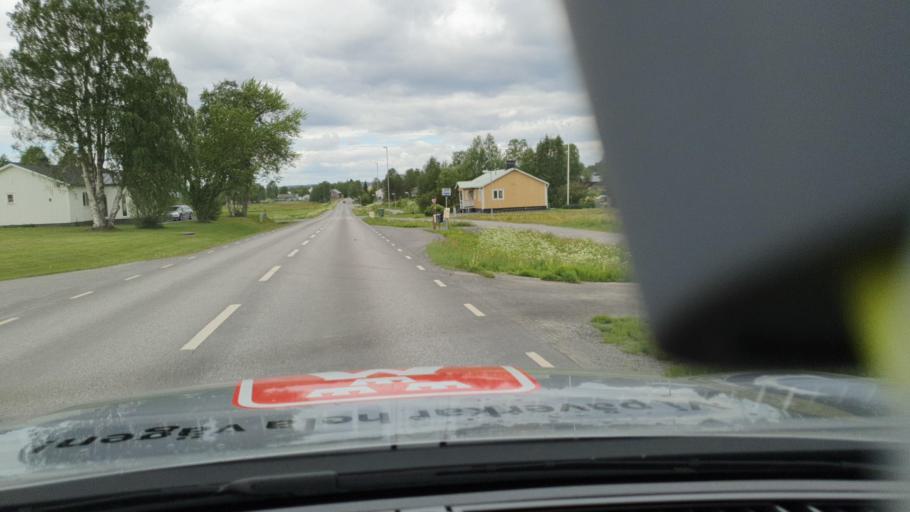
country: SE
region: Norrbotten
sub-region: Lulea Kommun
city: Gammelstad
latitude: 65.8064
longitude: 22.0288
